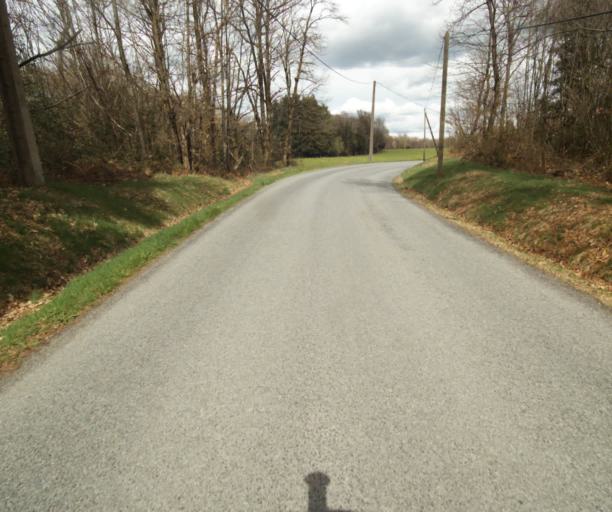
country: FR
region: Limousin
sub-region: Departement de la Correze
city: Argentat
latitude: 45.2051
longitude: 1.8952
